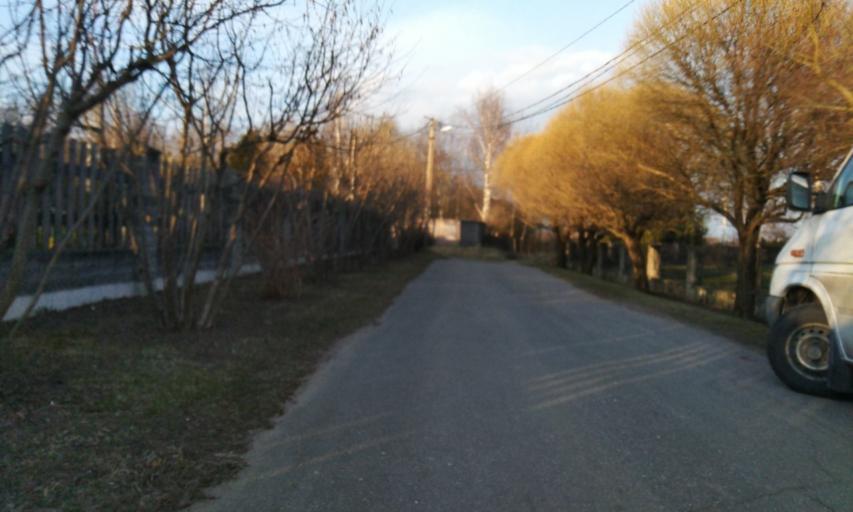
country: RU
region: Leningrad
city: Novoye Devyatkino
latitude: 60.0957
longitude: 30.4518
